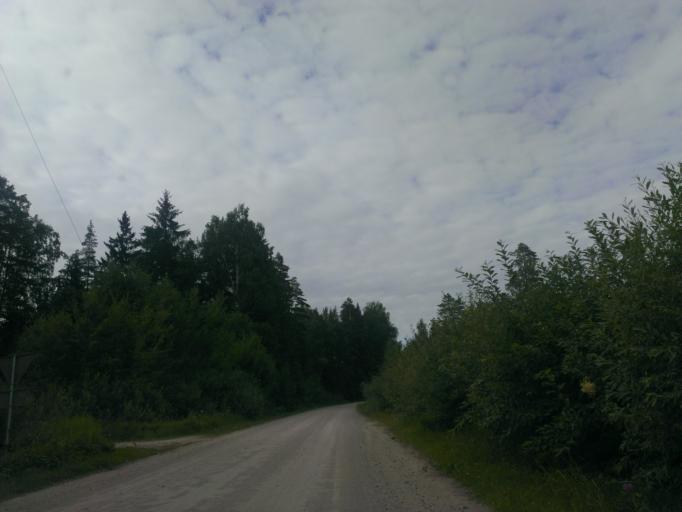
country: LV
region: Incukalns
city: Vangazi
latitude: 57.0947
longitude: 24.5626
